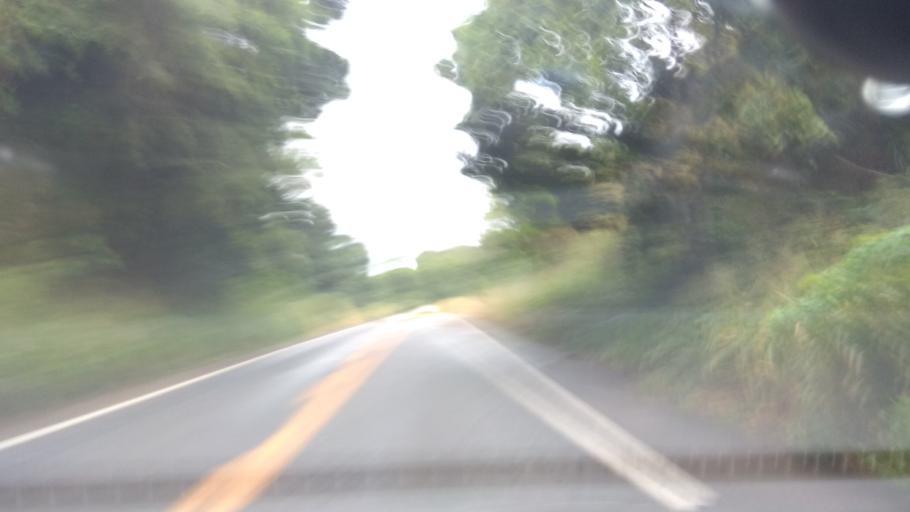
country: BR
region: Bahia
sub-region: Ubaitaba
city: Ubaitaba
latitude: -14.2623
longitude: -39.3408
